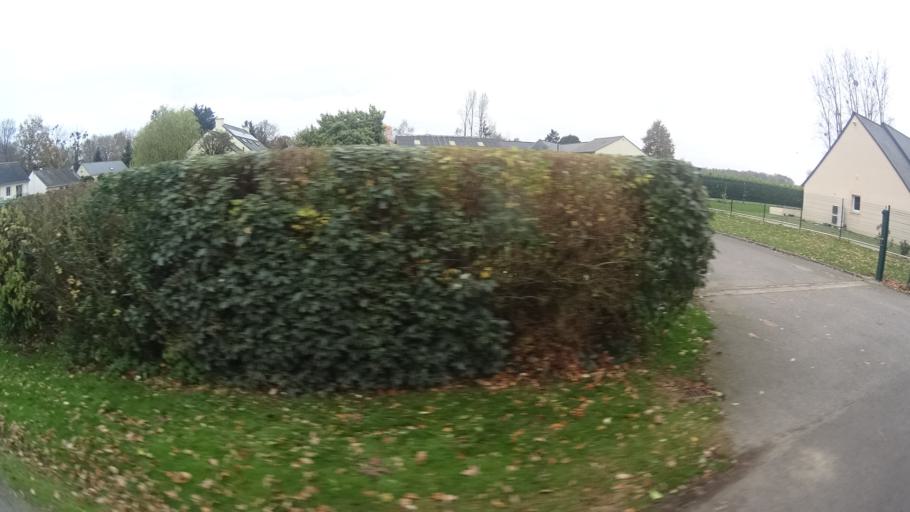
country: FR
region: Pays de la Loire
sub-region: Departement de la Loire-Atlantique
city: Avessac
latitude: 47.6712
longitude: -1.9131
